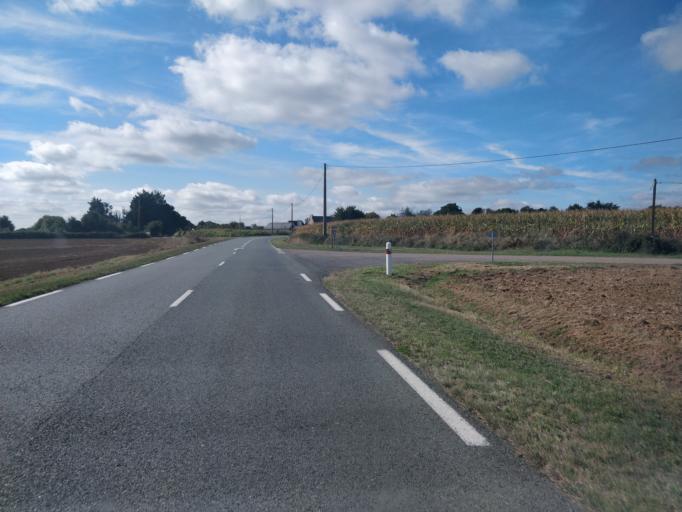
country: FR
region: Brittany
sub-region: Departement des Cotes-d'Armor
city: Erquy
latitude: 48.6006
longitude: -2.4713
